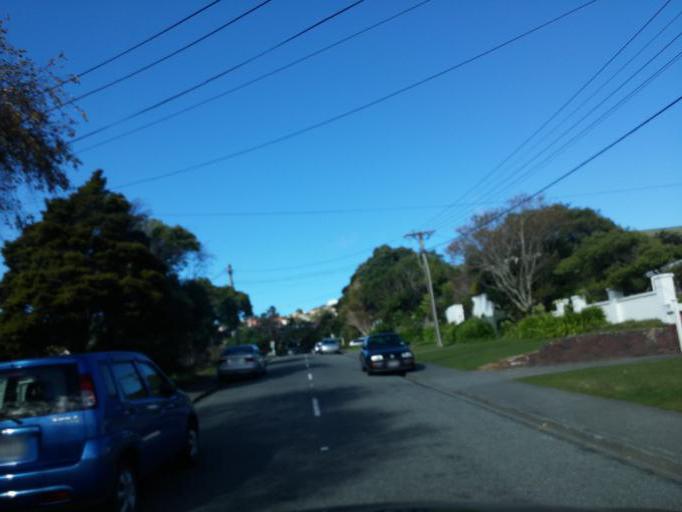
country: NZ
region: Wellington
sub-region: Wellington City
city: Kelburn
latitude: -41.2487
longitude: 174.7776
